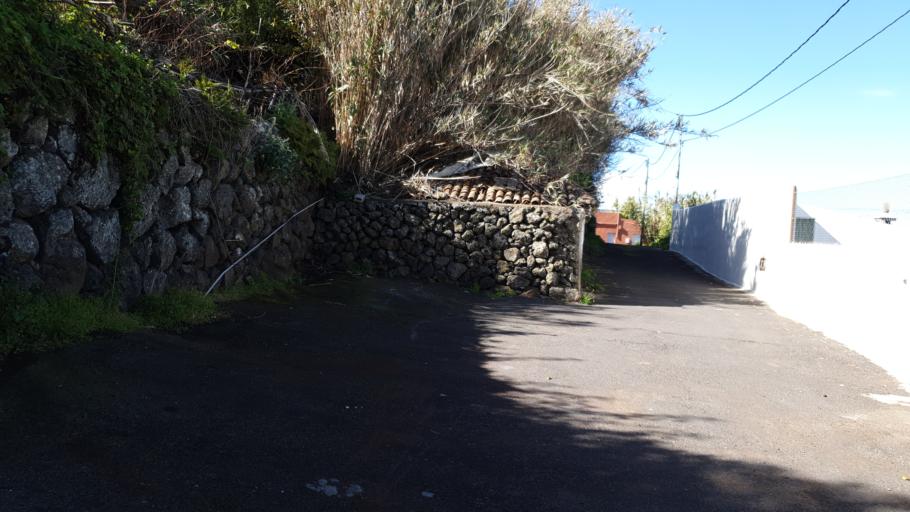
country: ES
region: Canary Islands
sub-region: Provincia de Santa Cruz de Tenerife
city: La Guancha
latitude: 28.3583
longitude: -16.6845
